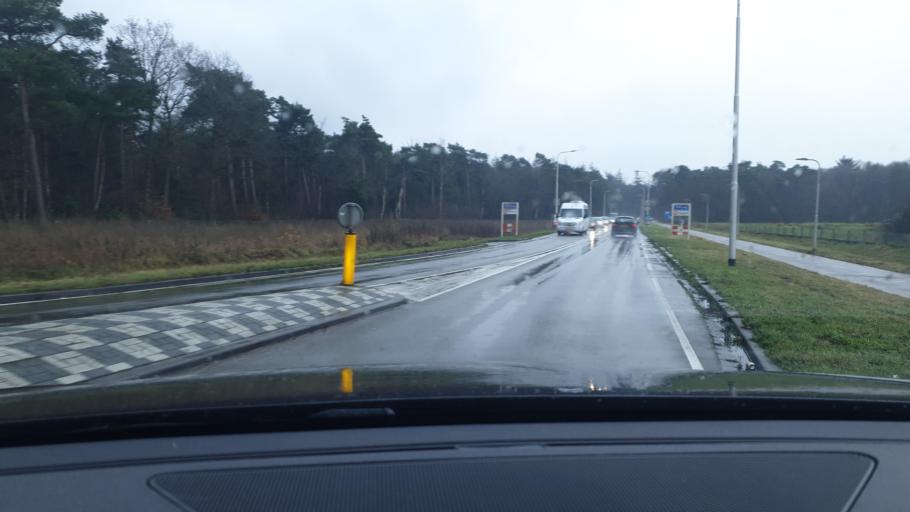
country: NL
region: North Brabant
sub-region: Gemeente Goirle
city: Goirle
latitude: 51.5671
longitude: 5.0172
